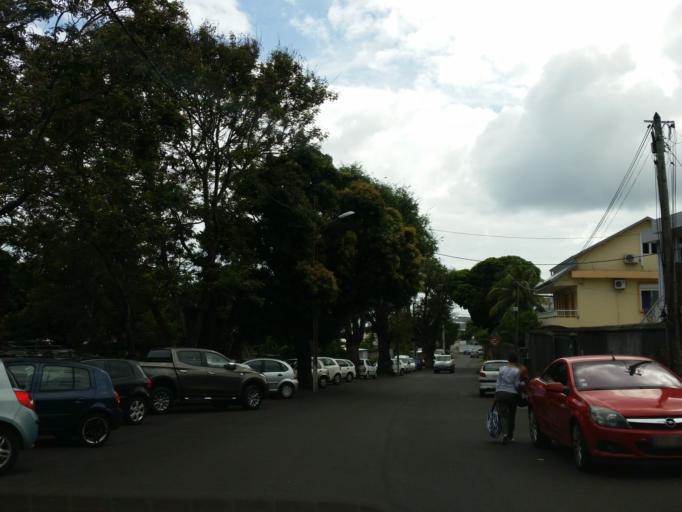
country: RE
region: Reunion
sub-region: Reunion
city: Saint-Denis
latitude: -20.8960
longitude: 55.4583
